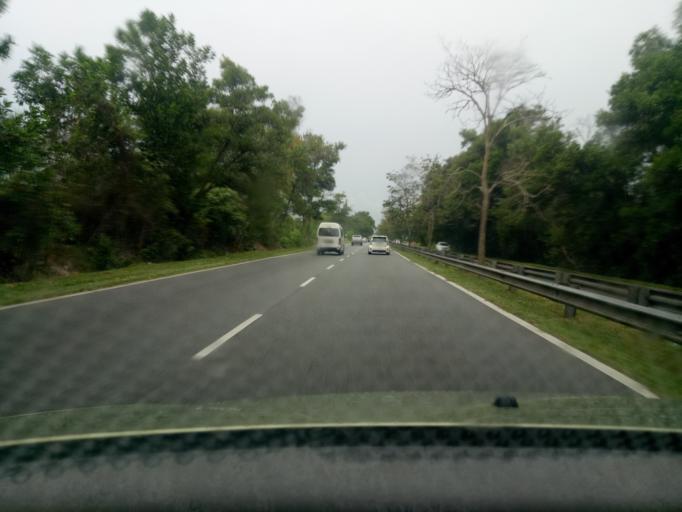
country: MY
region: Kedah
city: Sungai Petani
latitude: 5.6435
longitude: 100.5392
